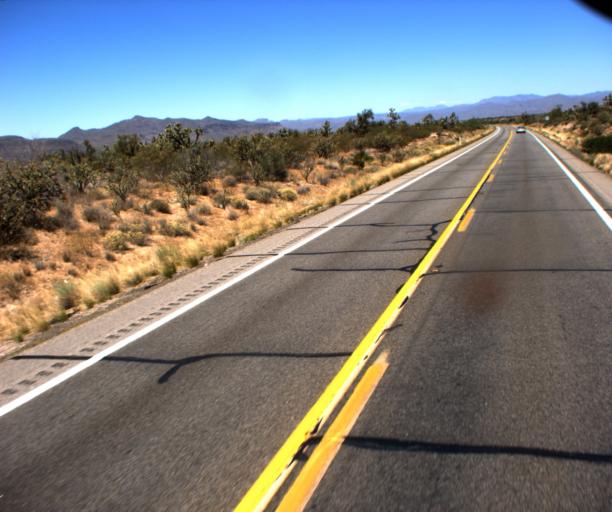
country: US
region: Arizona
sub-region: Yavapai County
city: Congress
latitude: 34.2655
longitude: -113.0909
